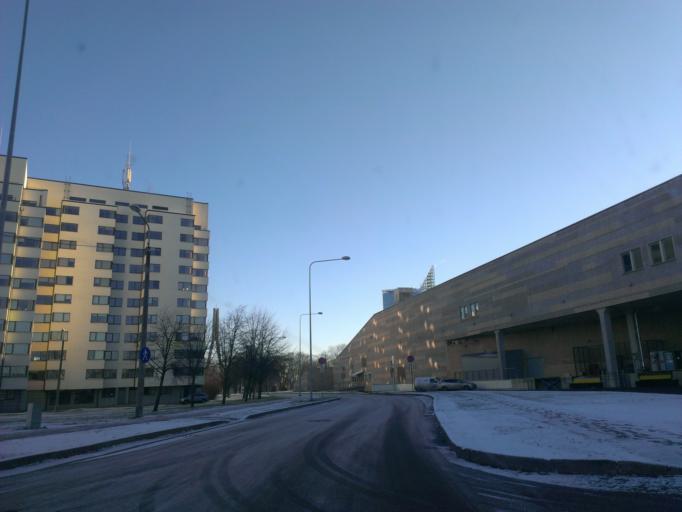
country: LV
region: Riga
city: Riga
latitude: 56.9506
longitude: 24.0810
